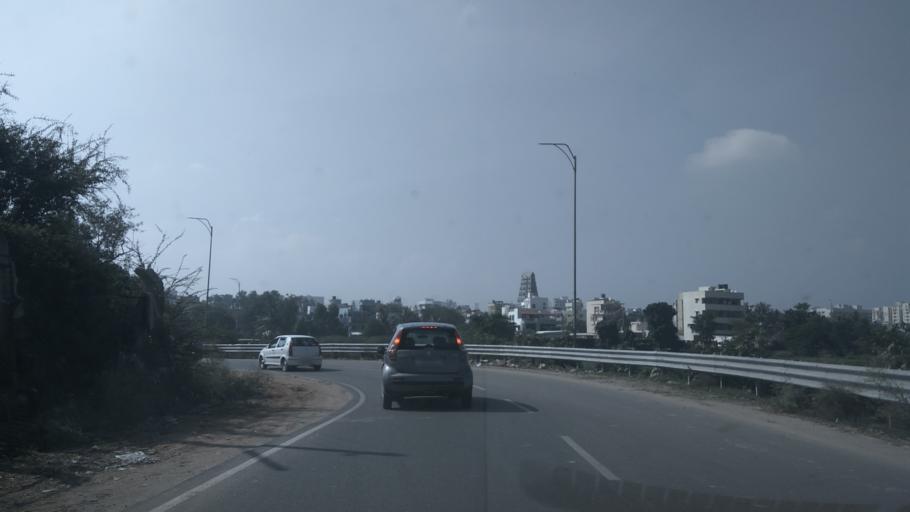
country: IN
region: Karnataka
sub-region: Bangalore Urban
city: Bangalore
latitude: 12.9330
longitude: 77.6770
